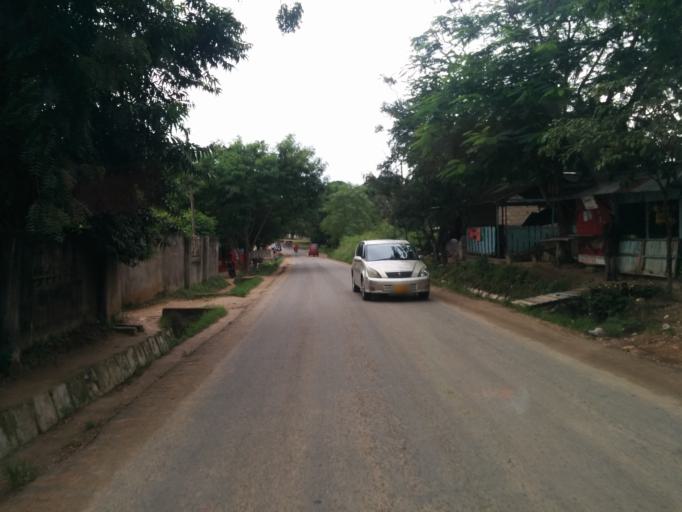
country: TZ
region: Dar es Salaam
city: Magomeni
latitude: -6.7698
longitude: 39.1938
